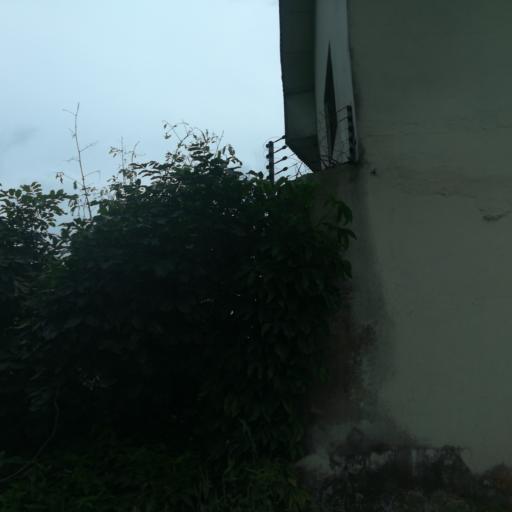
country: NG
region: Rivers
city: Port Harcourt
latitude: 4.8282
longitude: 7.0406
